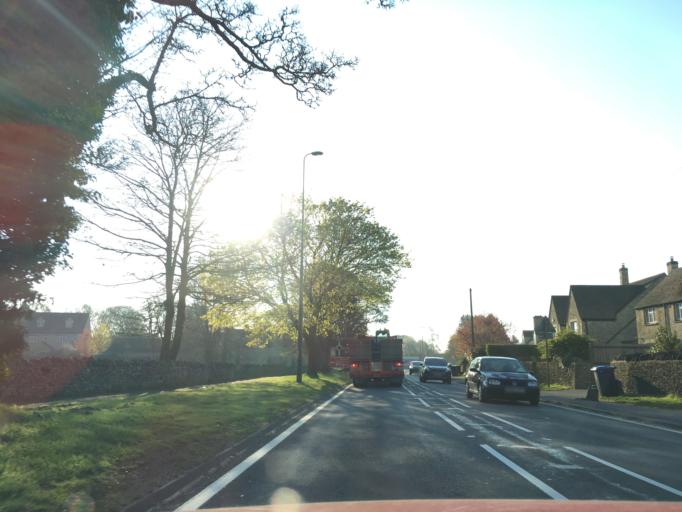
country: GB
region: England
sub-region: Oxfordshire
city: Burford
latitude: 51.8038
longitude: -1.6403
